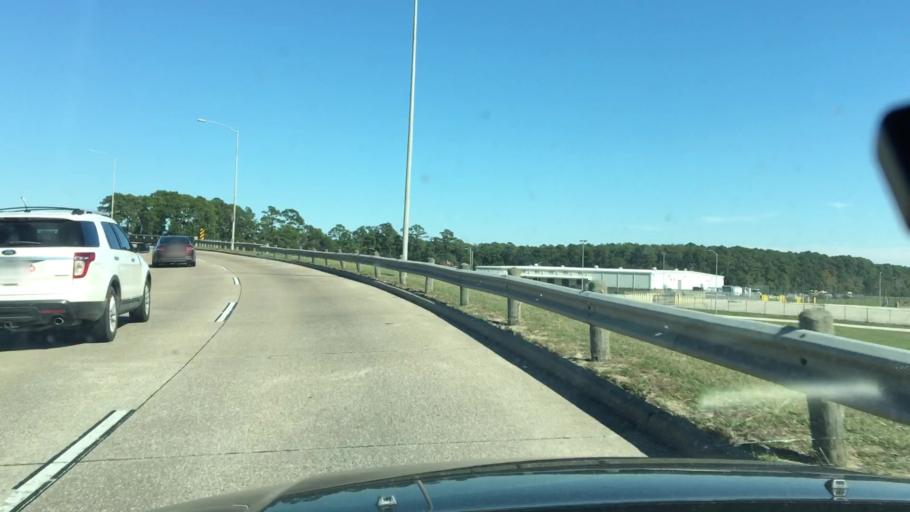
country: US
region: Texas
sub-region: Harris County
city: Humble
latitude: 29.9813
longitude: -95.3265
